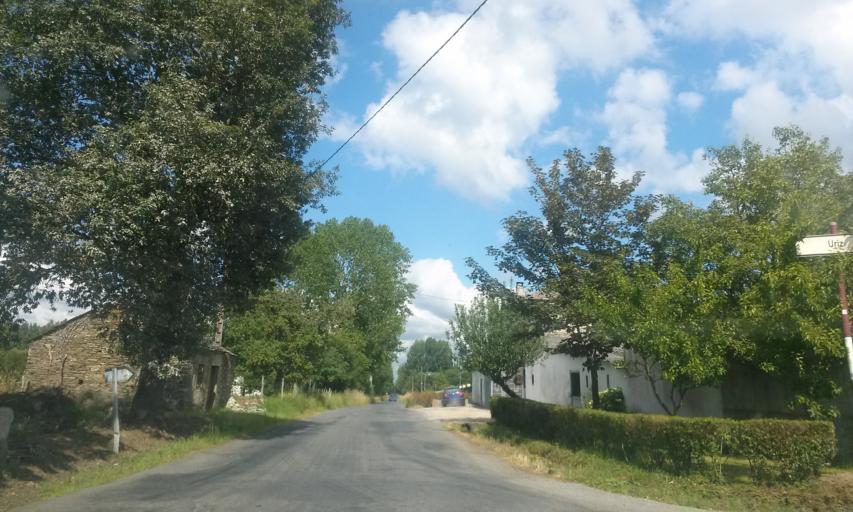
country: ES
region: Galicia
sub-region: Provincia de Lugo
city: Rabade
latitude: 43.1162
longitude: -7.6466
